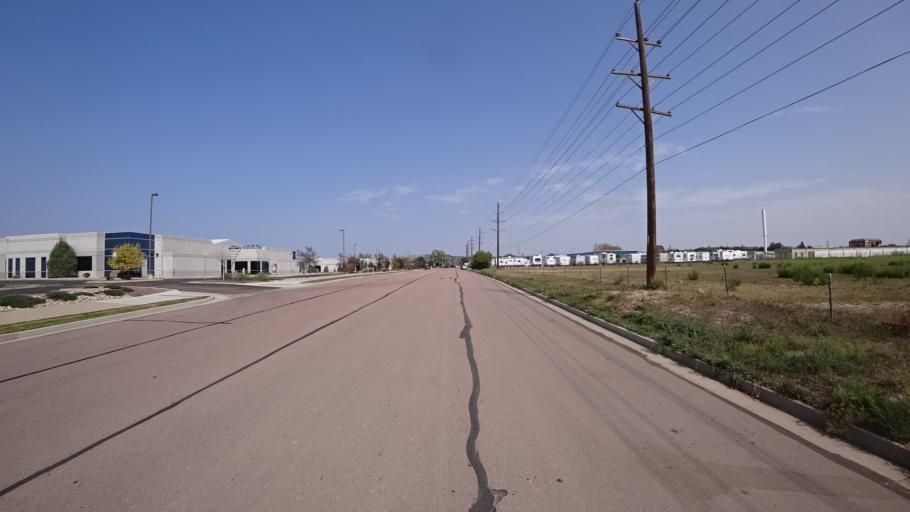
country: US
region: Colorado
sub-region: El Paso County
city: Cimarron Hills
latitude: 38.8371
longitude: -104.7387
